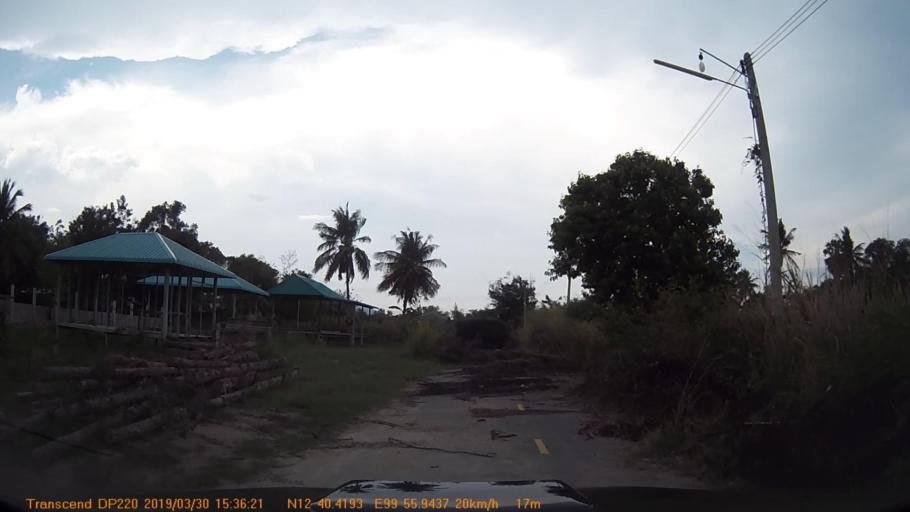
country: TH
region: Prachuap Khiri Khan
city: Hua Hin
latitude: 12.6736
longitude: 99.9324
